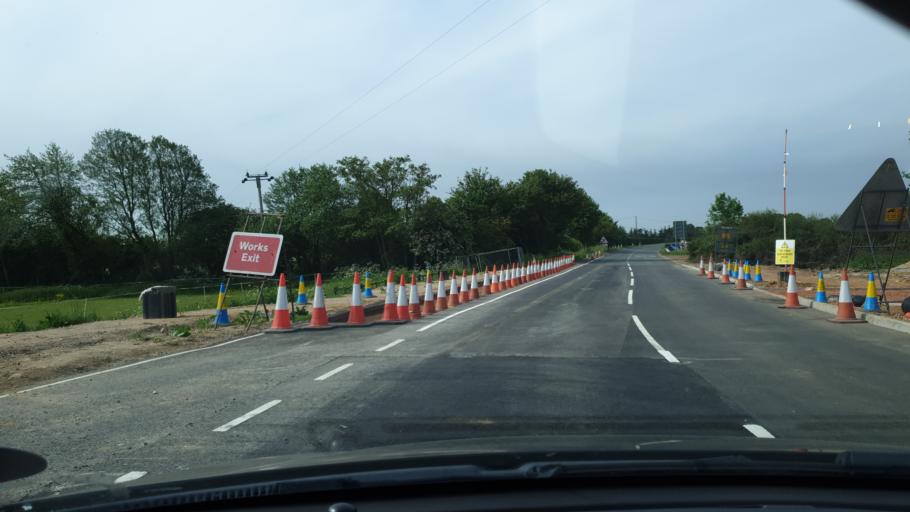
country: GB
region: England
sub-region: Essex
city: Great Bentley
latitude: 51.8860
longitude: 1.0593
